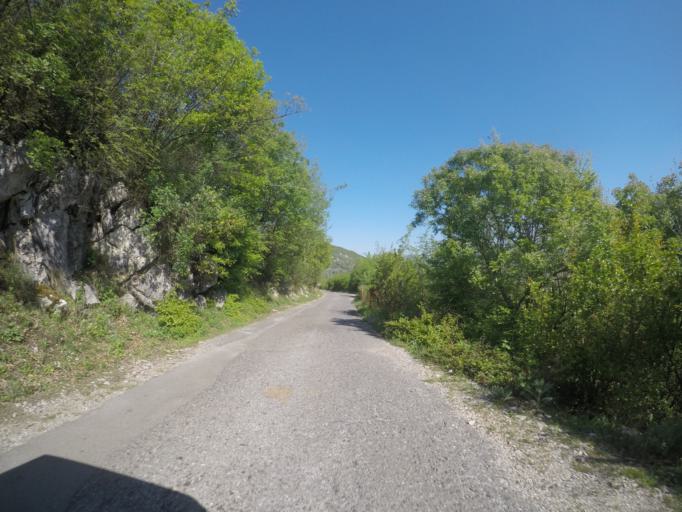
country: ME
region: Danilovgrad
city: Danilovgrad
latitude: 42.5282
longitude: 19.0934
